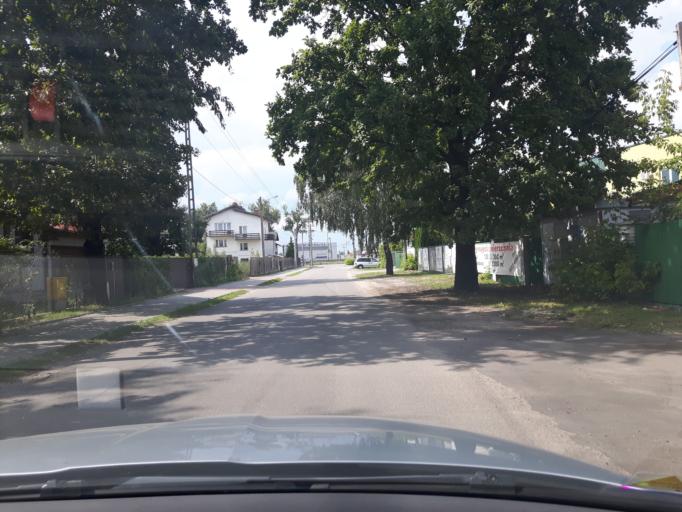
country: PL
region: Masovian Voivodeship
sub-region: Powiat wolominski
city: Marki
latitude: 52.3108
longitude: 21.0979
